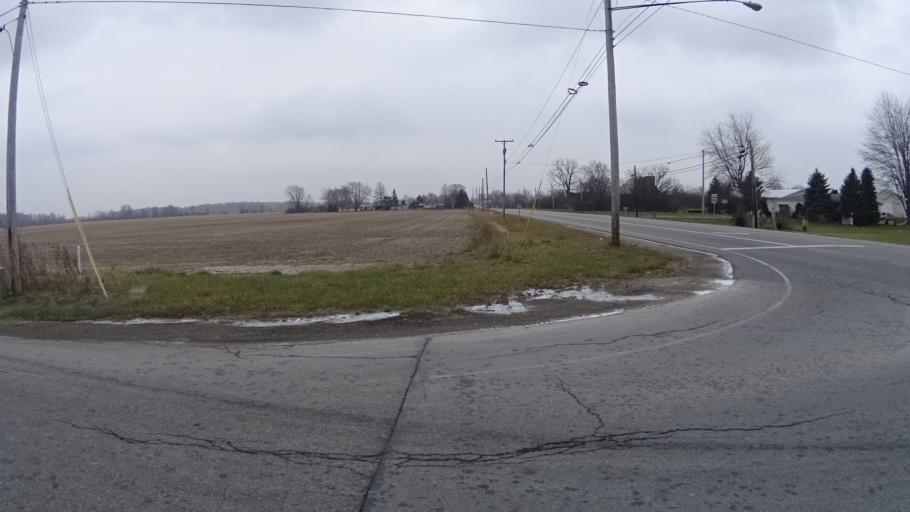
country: US
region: Ohio
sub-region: Lorain County
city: South Amherst
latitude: 41.3379
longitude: -82.2159
